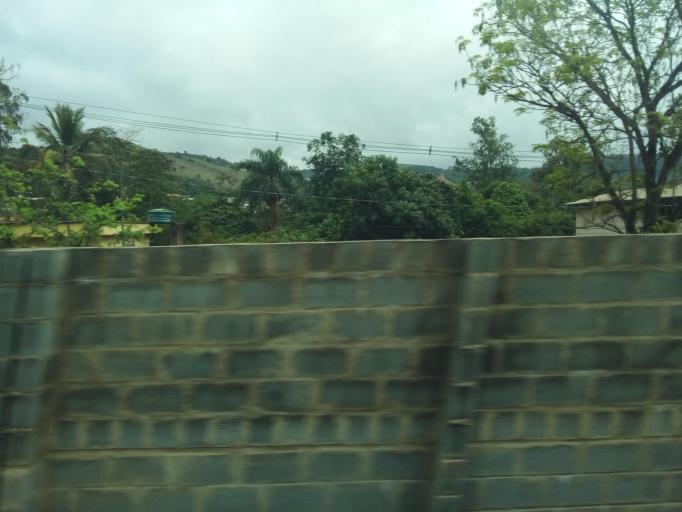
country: BR
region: Minas Gerais
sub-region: Rio Piracicaba
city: Rio Piracicaba
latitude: -19.9383
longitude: -43.1743
